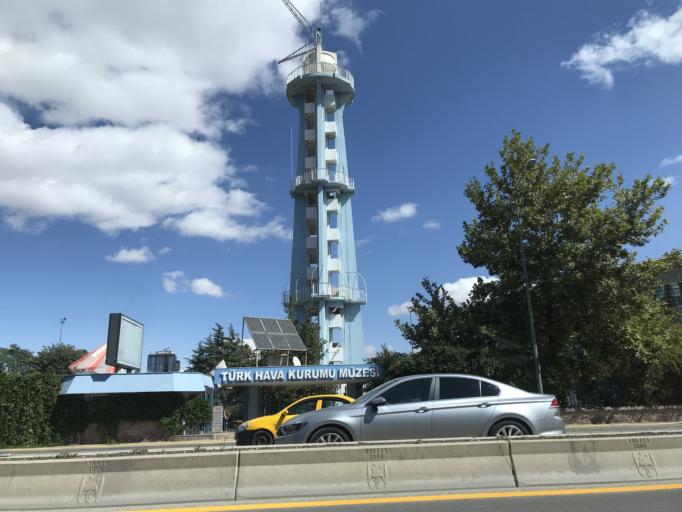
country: TR
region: Ankara
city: Ankara
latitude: 39.9378
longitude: 32.8421
